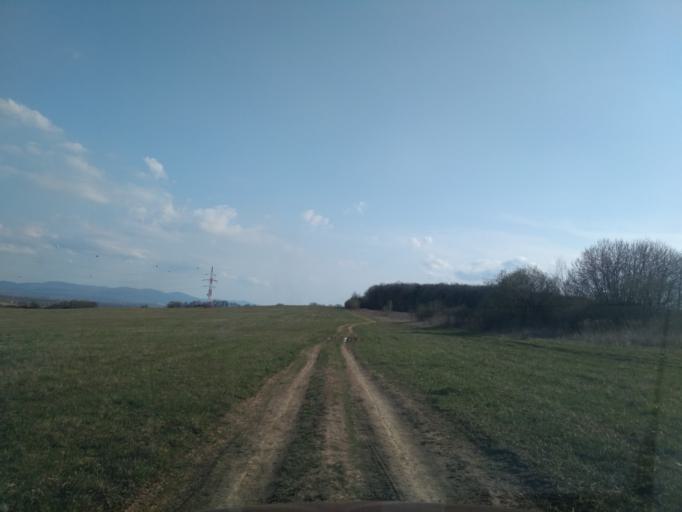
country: SK
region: Kosicky
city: Kosice
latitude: 48.6840
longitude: 21.1811
